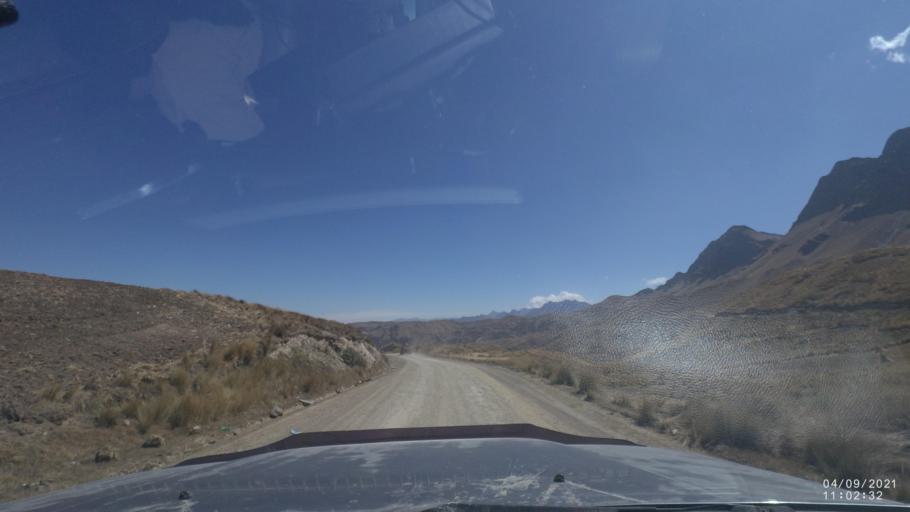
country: BO
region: Cochabamba
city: Sipe Sipe
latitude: -17.2842
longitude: -66.4585
